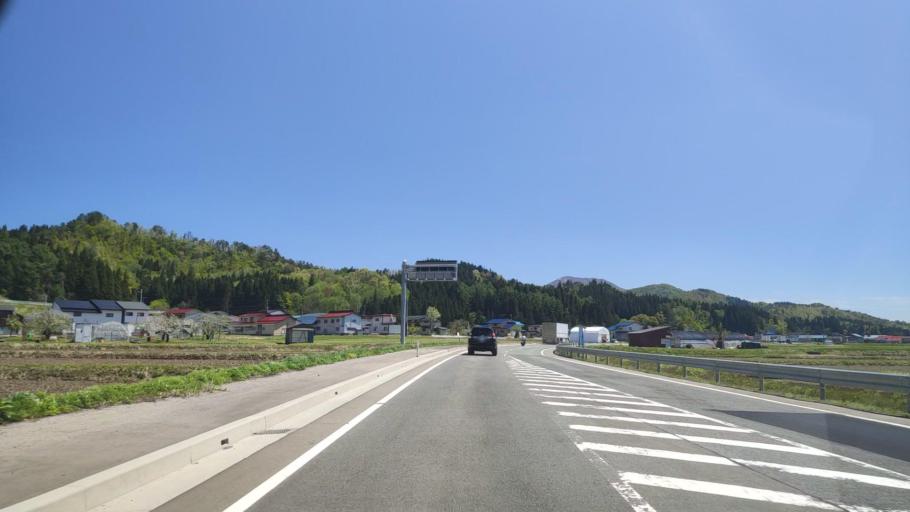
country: JP
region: Yamagata
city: Obanazawa
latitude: 38.5604
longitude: 140.3995
